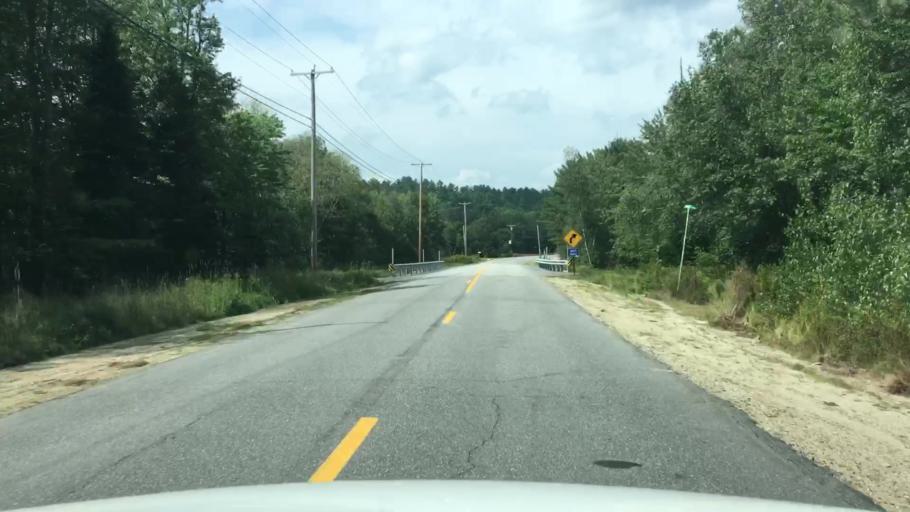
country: US
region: Maine
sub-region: Oxford County
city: Rumford
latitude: 44.5265
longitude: -70.6369
